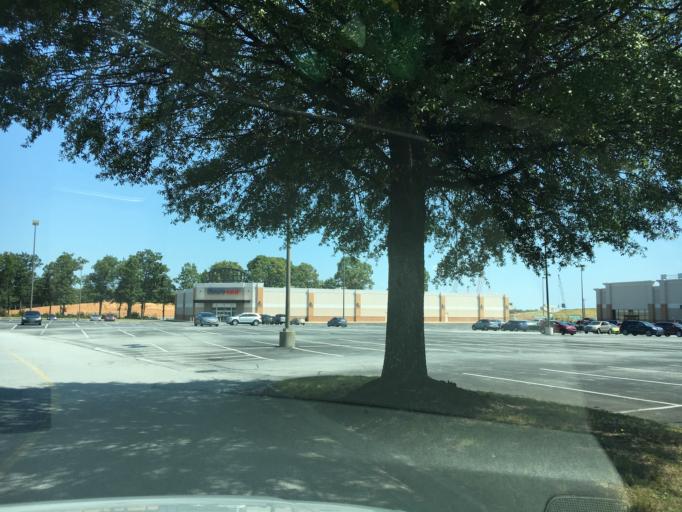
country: US
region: South Carolina
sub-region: Greenville County
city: Mauldin
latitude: 34.8324
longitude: -82.3036
